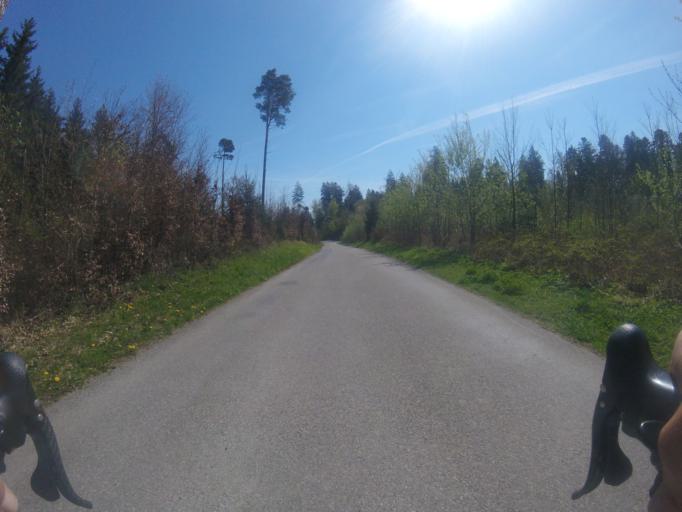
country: CH
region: Fribourg
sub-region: Sense District
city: Flamatt
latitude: 46.9153
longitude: 7.3396
